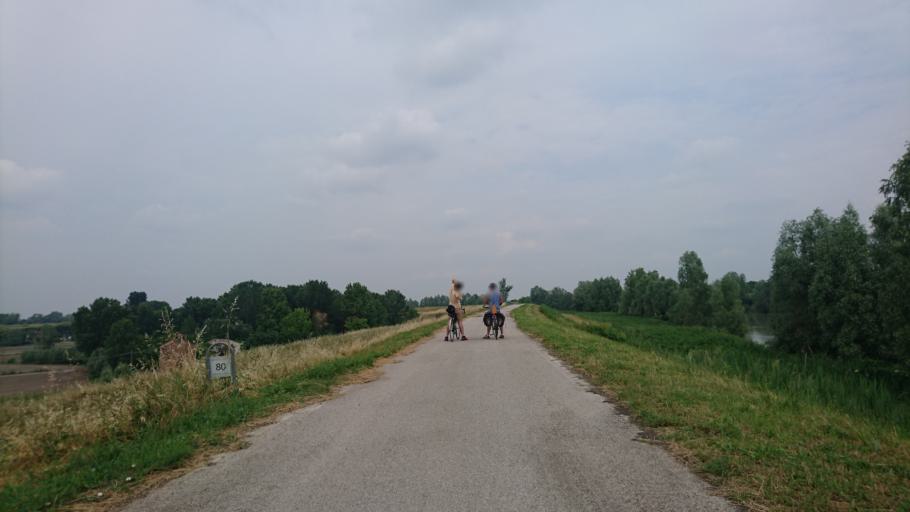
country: IT
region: Veneto
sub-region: Provincia di Padova
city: Piacenza d'Adige
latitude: 45.1199
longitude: 11.5807
